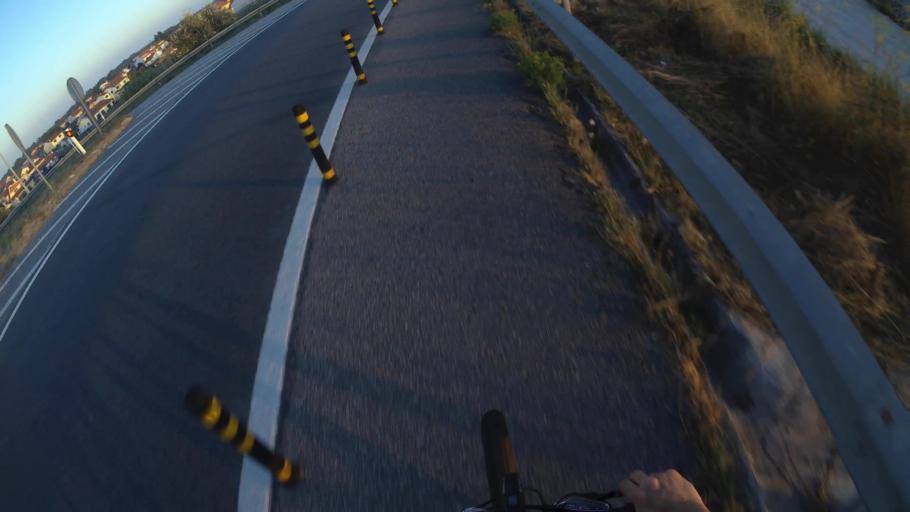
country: PT
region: Aveiro
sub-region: Ilhavo
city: Gafanha da Encarnacao
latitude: 40.6277
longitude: -8.7330
